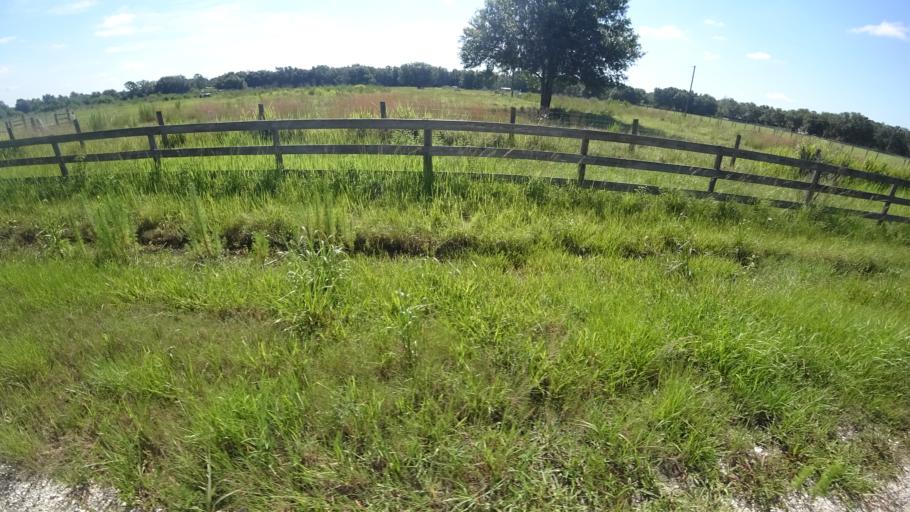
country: US
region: Florida
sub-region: Sarasota County
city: The Meadows
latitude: 27.4362
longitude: -82.3200
